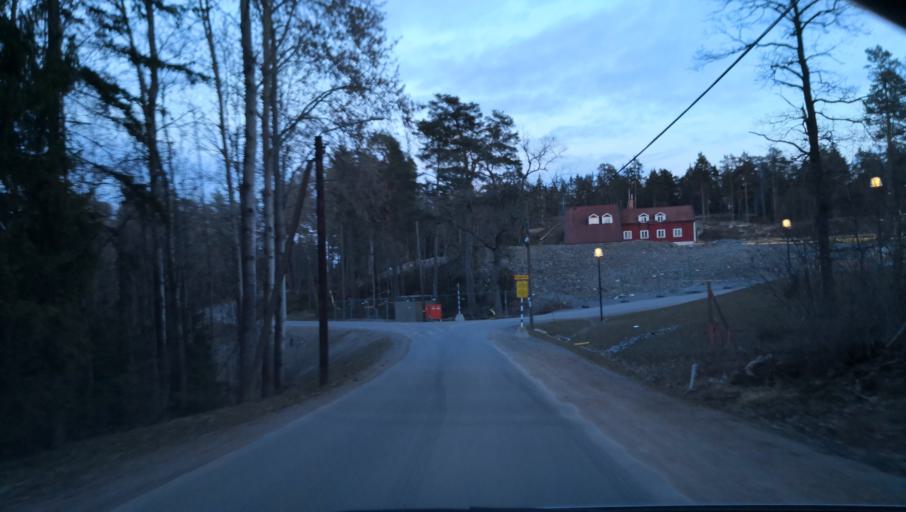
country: SE
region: Stockholm
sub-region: Nacka Kommun
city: Boo
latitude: 59.3288
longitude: 18.3213
